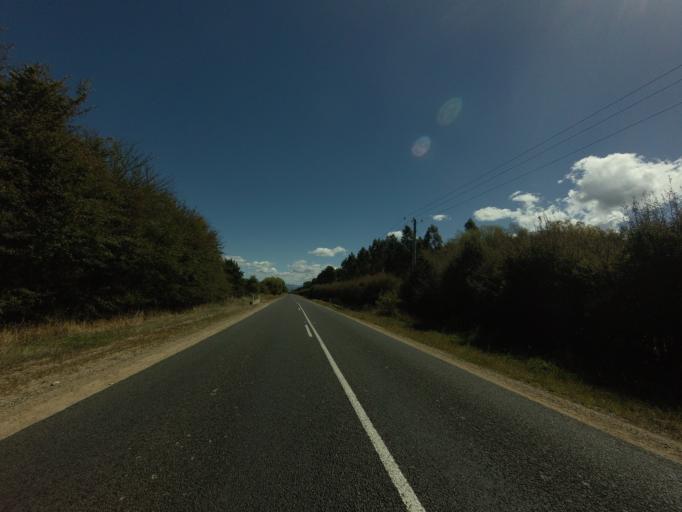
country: AU
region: Tasmania
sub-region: Break O'Day
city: St Helens
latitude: -41.5783
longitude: 148.1479
